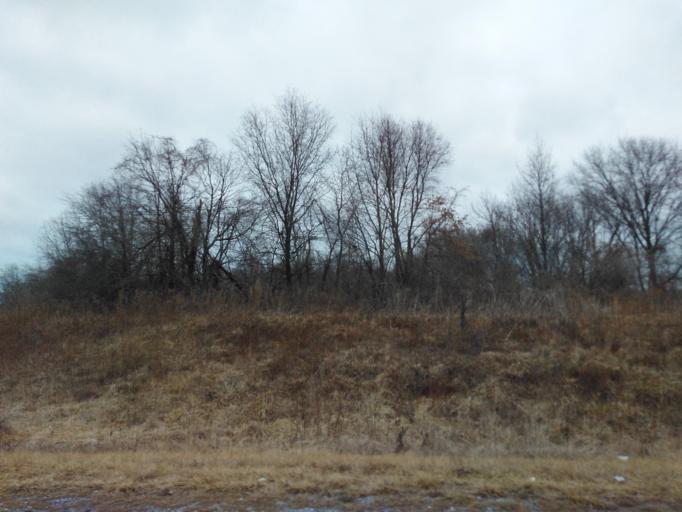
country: US
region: Illinois
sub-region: Madison County
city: Saint Jacob
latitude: 38.7192
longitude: -89.8005
